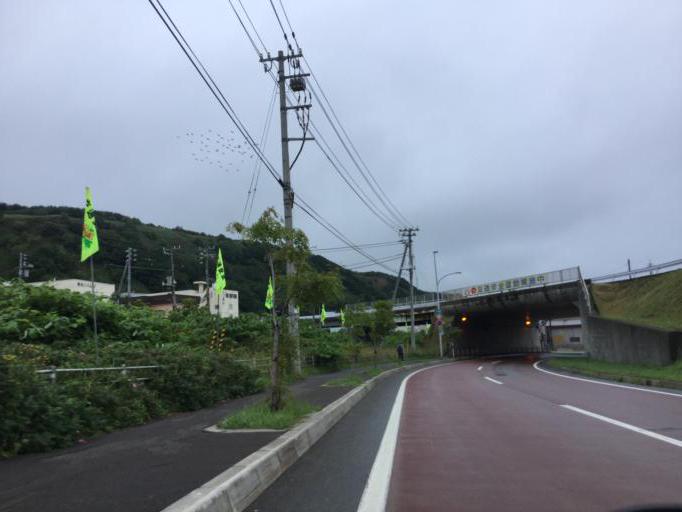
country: JP
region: Hokkaido
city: Wakkanai
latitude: 45.4047
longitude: 141.6756
